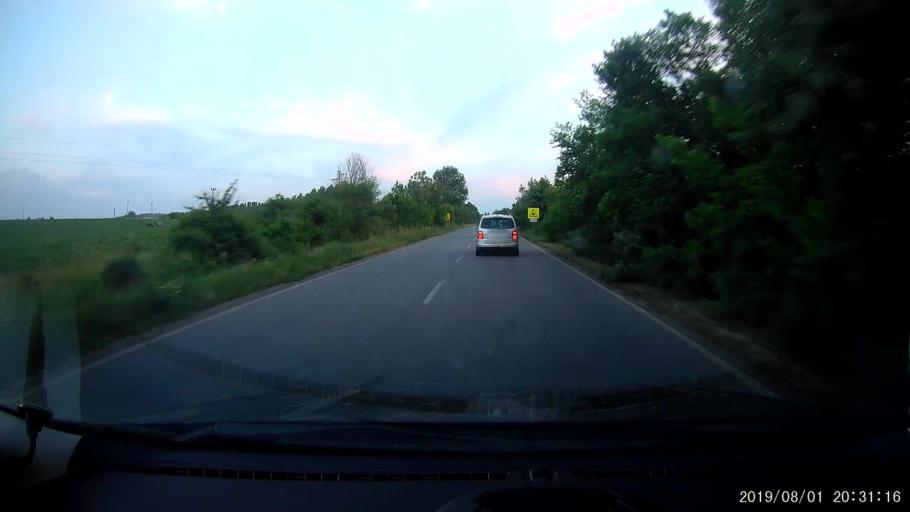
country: BG
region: Yambol
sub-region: Obshtina Elkhovo
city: Elkhovo
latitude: 42.1302
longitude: 26.5408
